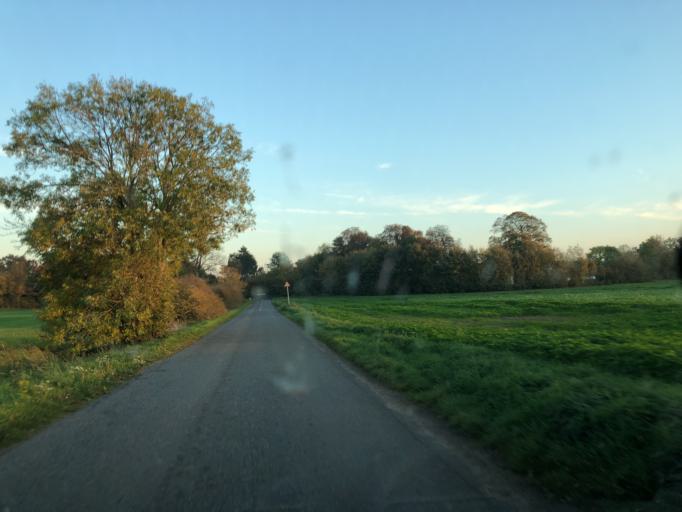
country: DK
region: South Denmark
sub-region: Vejle Kommune
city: Borkop
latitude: 55.6125
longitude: 9.6469
